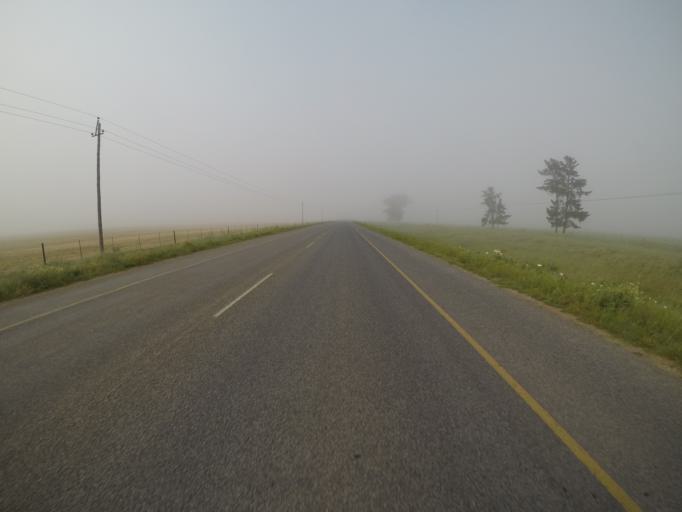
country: ZA
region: Western Cape
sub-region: City of Cape Town
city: Kraaifontein
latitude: -33.6717
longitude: 18.7071
